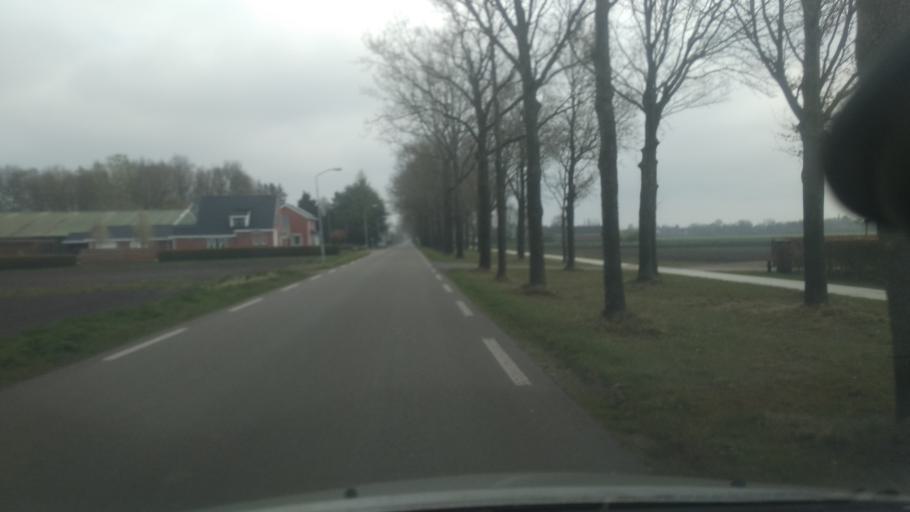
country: NL
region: Groningen
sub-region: Gemeente Stadskanaal
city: Stadskanaal
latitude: 52.9324
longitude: 6.9944
